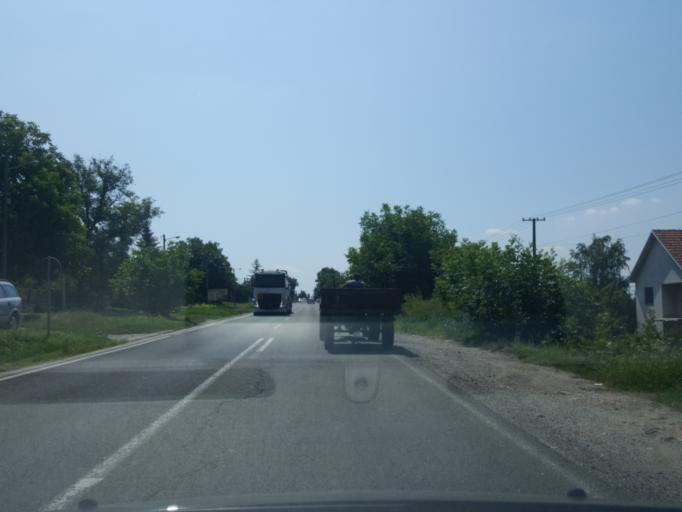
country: RS
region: Central Serbia
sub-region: Belgrade
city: Mladenovac
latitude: 44.4551
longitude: 20.6778
